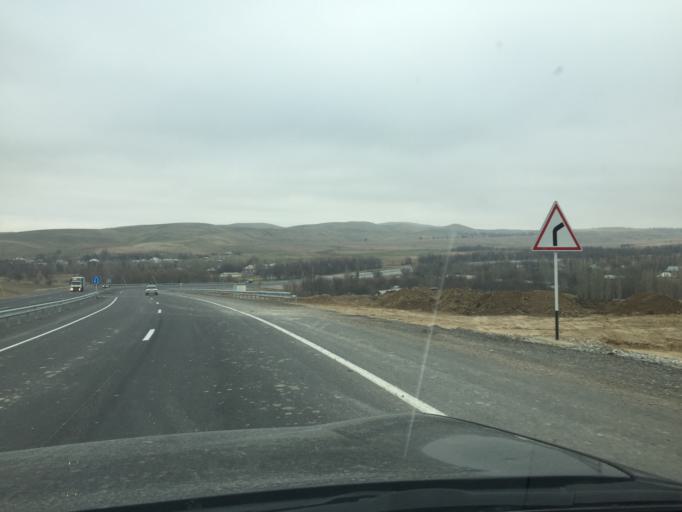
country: KZ
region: Ongtustik Qazaqstan
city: Sastobe
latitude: 42.4955
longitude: 69.9597
